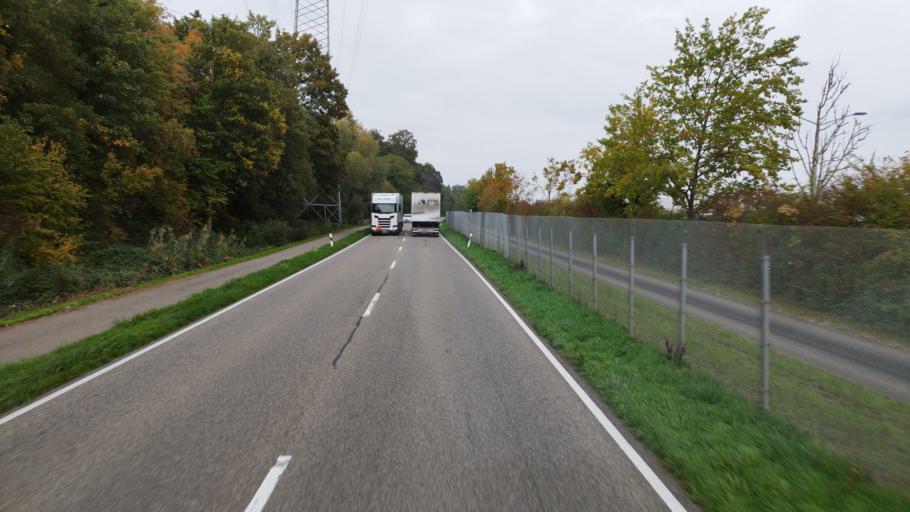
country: DE
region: Baden-Wuerttemberg
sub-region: Karlsruhe Region
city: Rheinau
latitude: 48.8619
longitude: 8.1720
